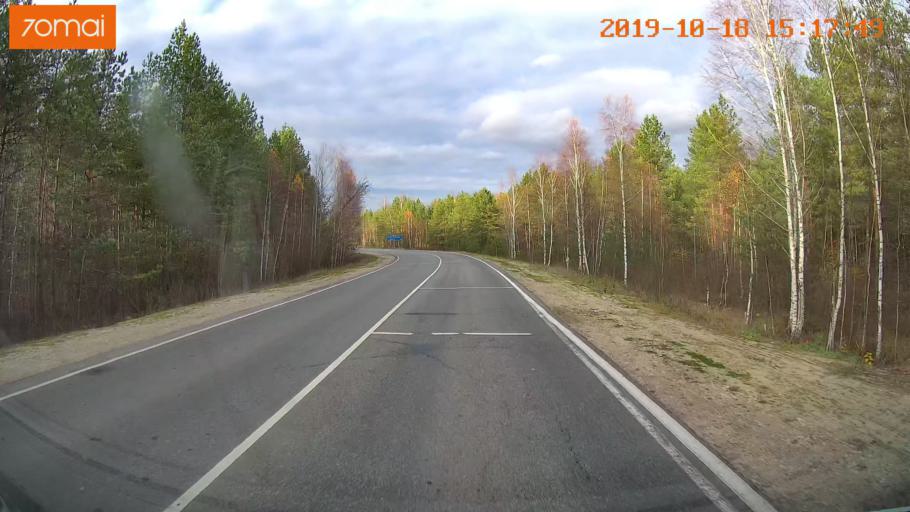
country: RU
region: Vladimir
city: Anopino
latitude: 55.6554
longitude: 40.7273
